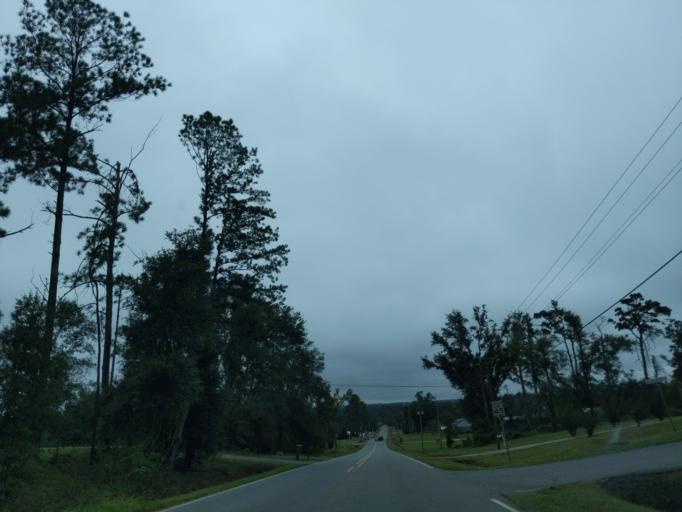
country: US
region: Florida
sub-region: Jackson County
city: Sneads
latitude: 30.7175
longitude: -84.9325
